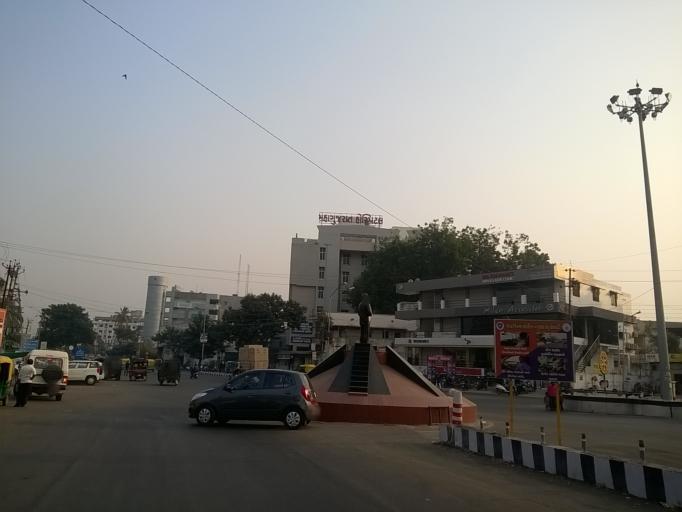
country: IN
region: Gujarat
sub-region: Kheda
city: Nadiad
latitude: 22.6898
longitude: 72.8715
